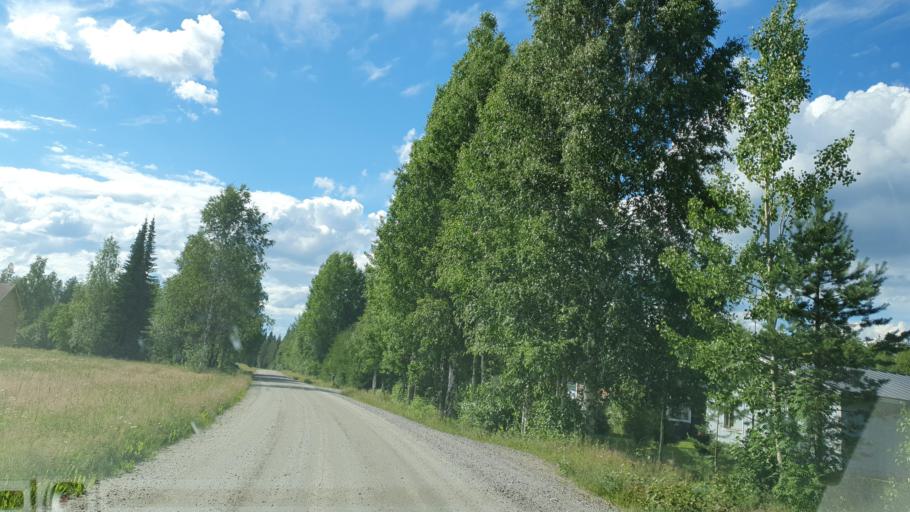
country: FI
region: Kainuu
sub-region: Kehys-Kainuu
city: Kuhmo
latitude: 64.1505
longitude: 29.7426
